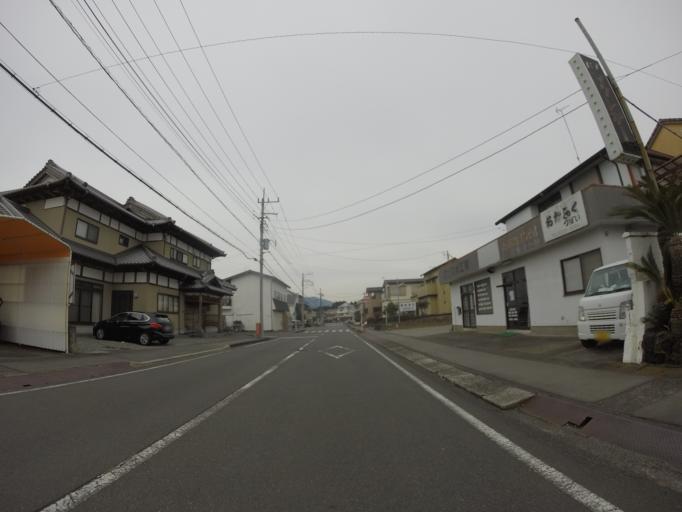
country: JP
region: Shizuoka
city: Fujinomiya
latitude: 35.2497
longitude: 138.6378
